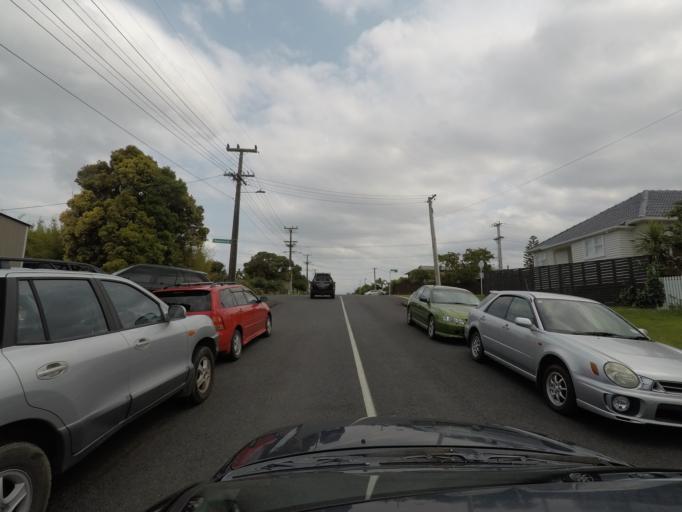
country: NZ
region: Auckland
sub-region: Auckland
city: Rosebank
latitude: -36.8265
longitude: 174.6464
